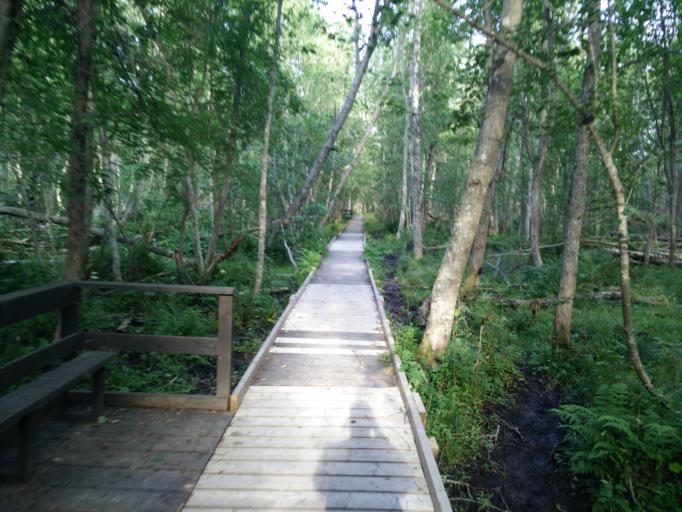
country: SE
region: Vaesternorrland
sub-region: Timra Kommun
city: Soraker
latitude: 62.4506
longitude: 17.4857
